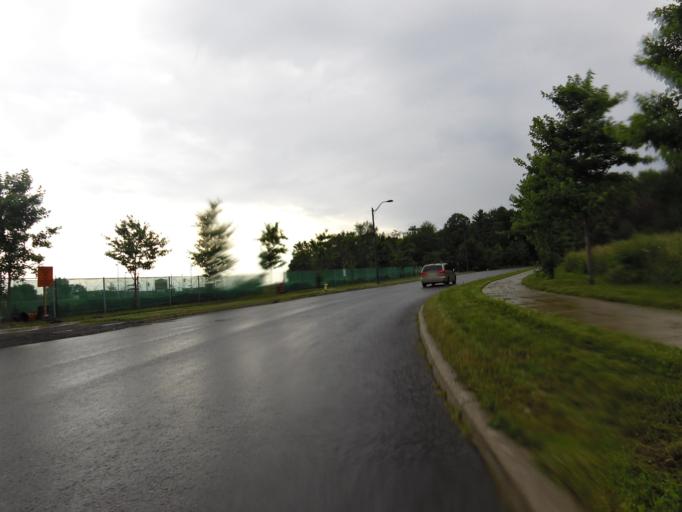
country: CA
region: Ontario
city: Bells Corners
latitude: 45.3132
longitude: -75.9036
